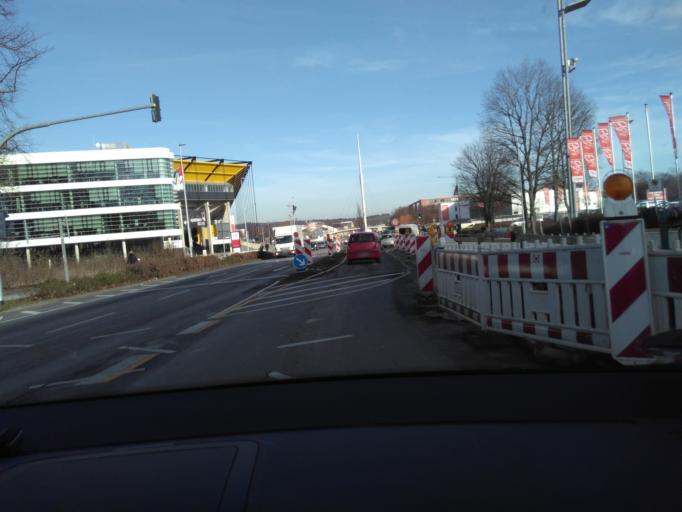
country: DE
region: North Rhine-Westphalia
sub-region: Regierungsbezirk Koln
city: Aachen
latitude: 50.7909
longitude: 6.0972
